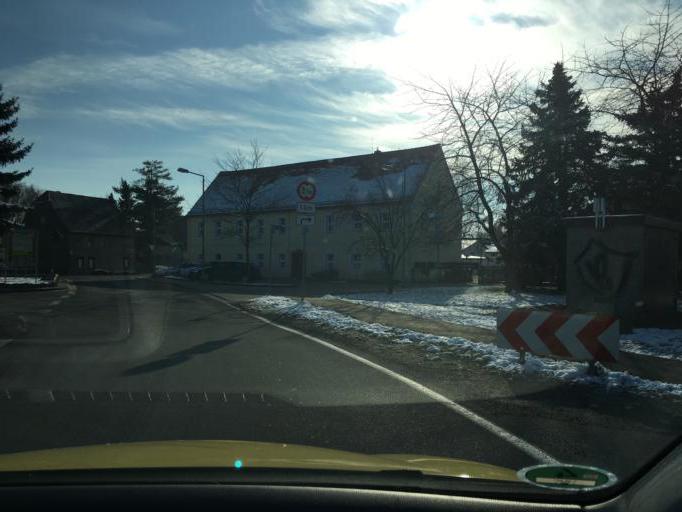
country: DE
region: Saxony
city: Belgershain
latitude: 51.2378
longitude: 12.5486
